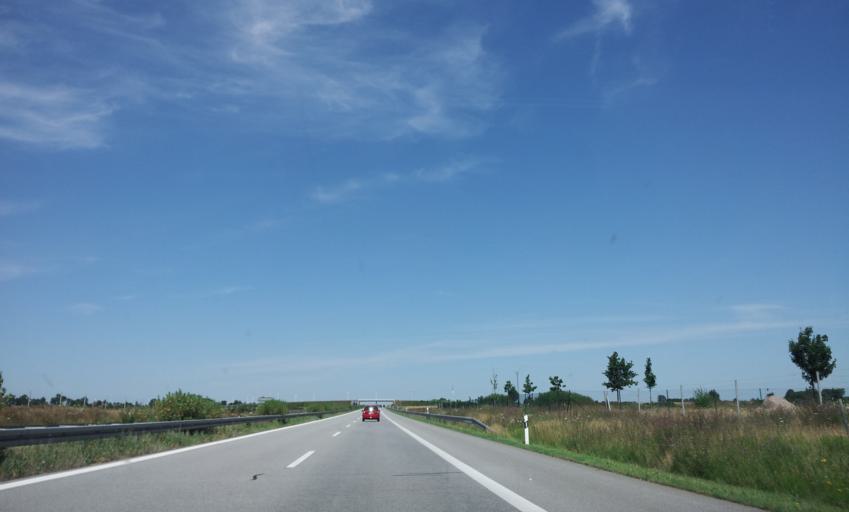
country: DE
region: Mecklenburg-Vorpommern
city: Burow
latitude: 53.8296
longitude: 13.3261
